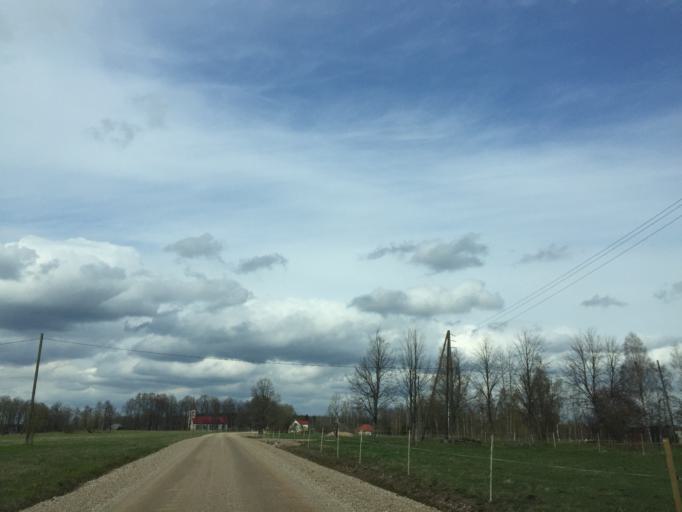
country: LV
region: Ligatne
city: Ligatne
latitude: 57.2129
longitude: 25.0675
